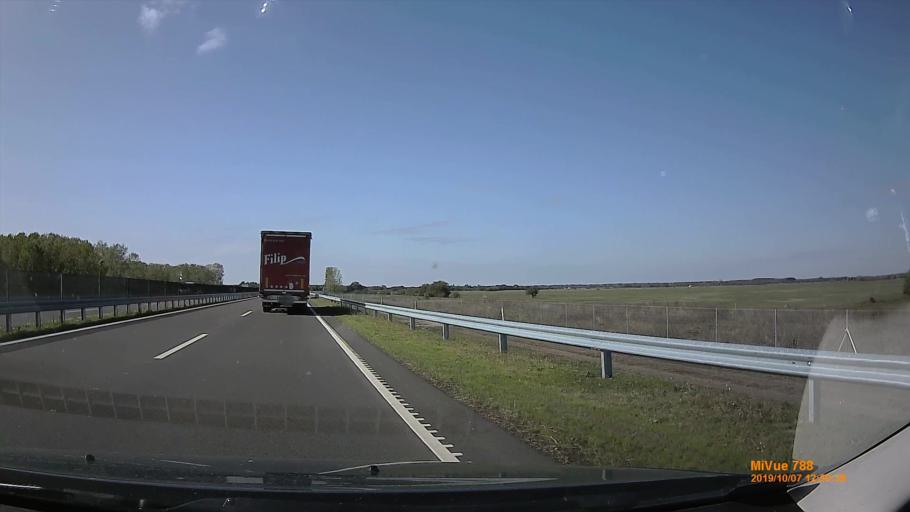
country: HU
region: Jasz-Nagykun-Szolnok
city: Cserkeszolo
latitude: 46.8845
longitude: 20.2062
